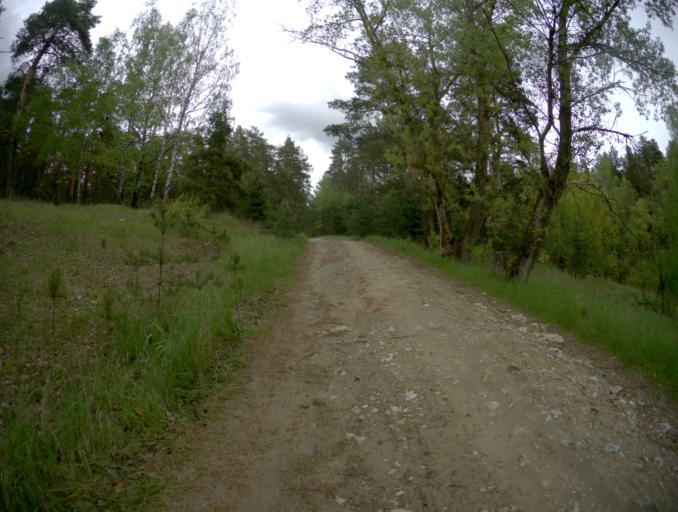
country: RU
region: Rjazan
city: Syntul
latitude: 54.9917
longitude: 41.2182
